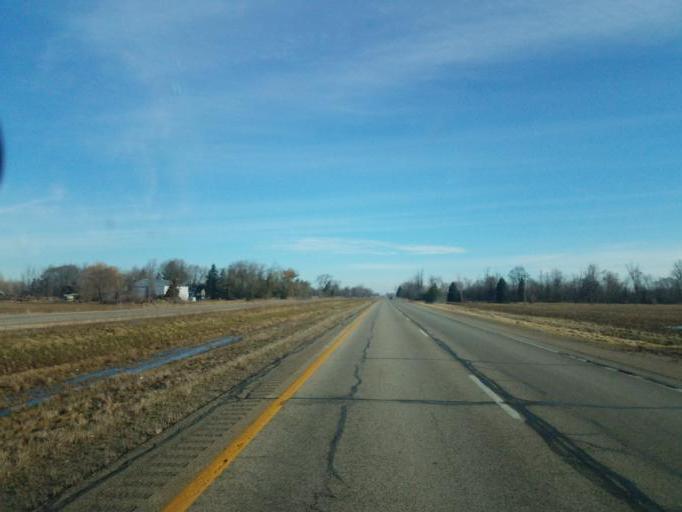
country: US
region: Michigan
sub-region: Gratiot County
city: Ithaca
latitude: 43.1988
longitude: -84.5633
